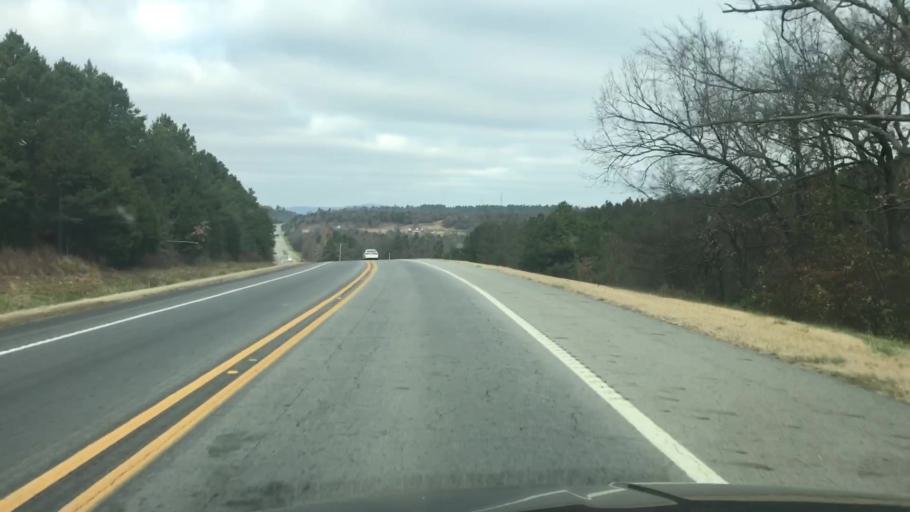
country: US
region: Arkansas
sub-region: Scott County
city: Waldron
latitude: 34.8429
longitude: -94.0546
